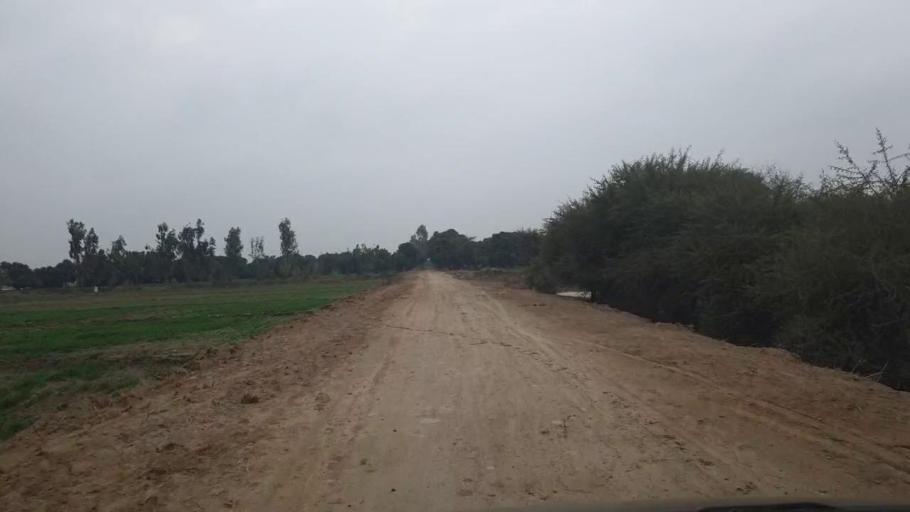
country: PK
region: Sindh
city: Shahdadpur
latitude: 25.8628
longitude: 68.6978
